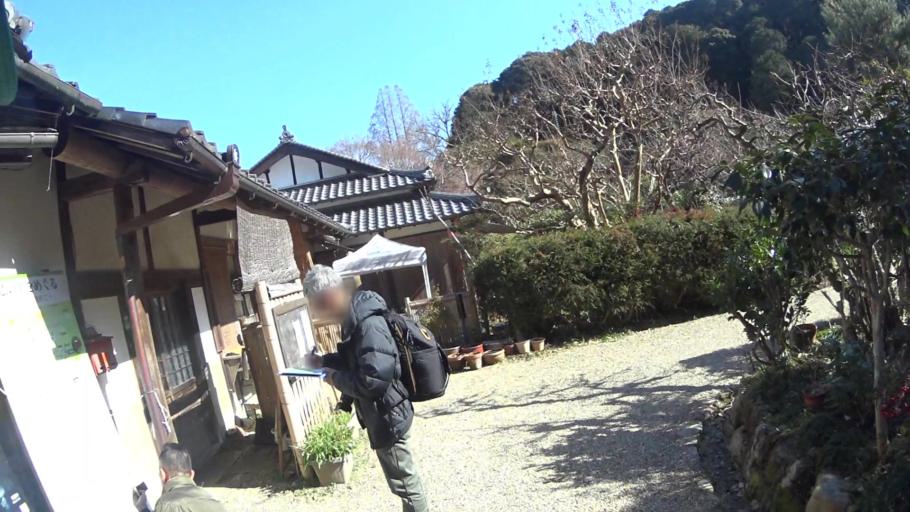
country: JP
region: Nara
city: Nara-shi
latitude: 34.7160
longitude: 135.8727
